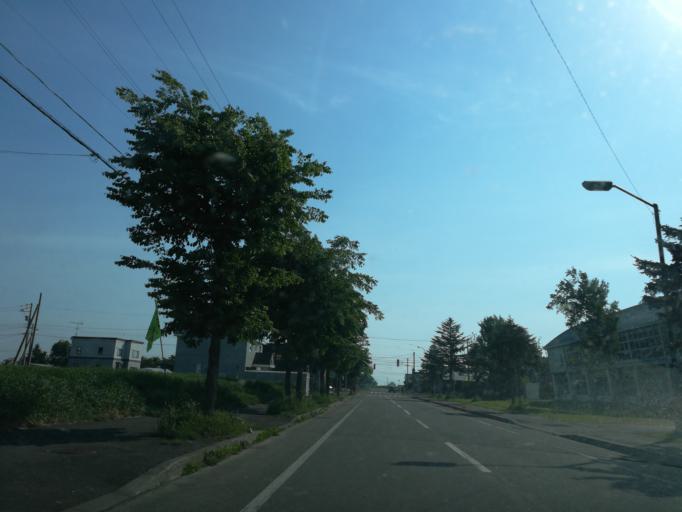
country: JP
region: Hokkaido
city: Iwamizawa
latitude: 43.1729
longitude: 141.7102
